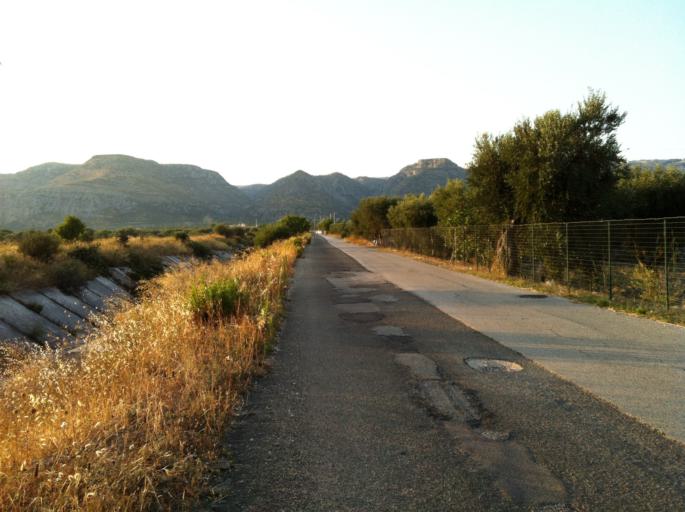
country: IT
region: Apulia
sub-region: Provincia di Foggia
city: Manfredonia
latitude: 41.6558
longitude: 15.9518
